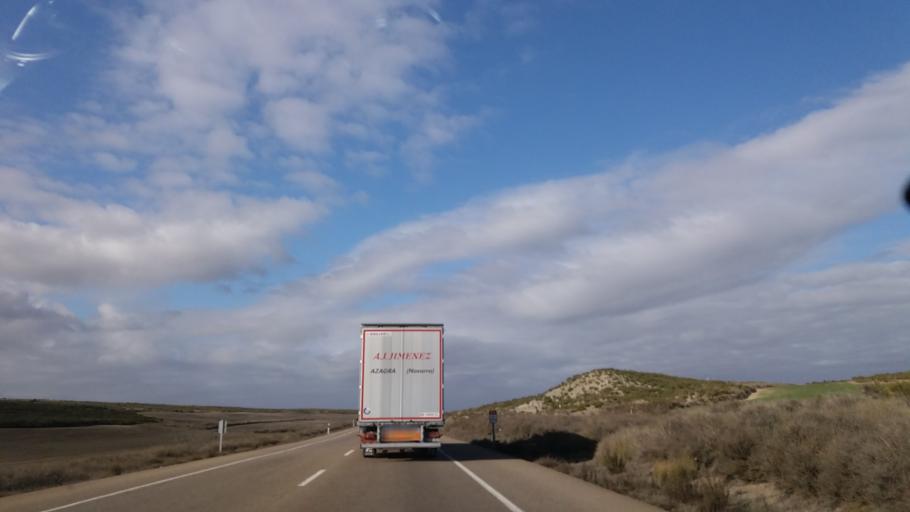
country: ES
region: Aragon
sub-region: Provincia de Zaragoza
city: Gelsa
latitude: 41.5015
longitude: -0.3806
